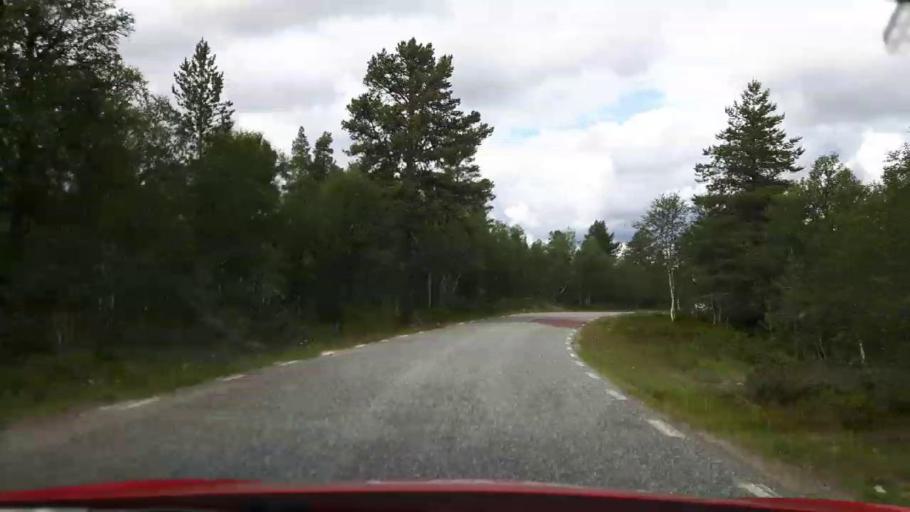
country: NO
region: Hedmark
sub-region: Trysil
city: Innbygda
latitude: 62.1194
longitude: 12.9717
